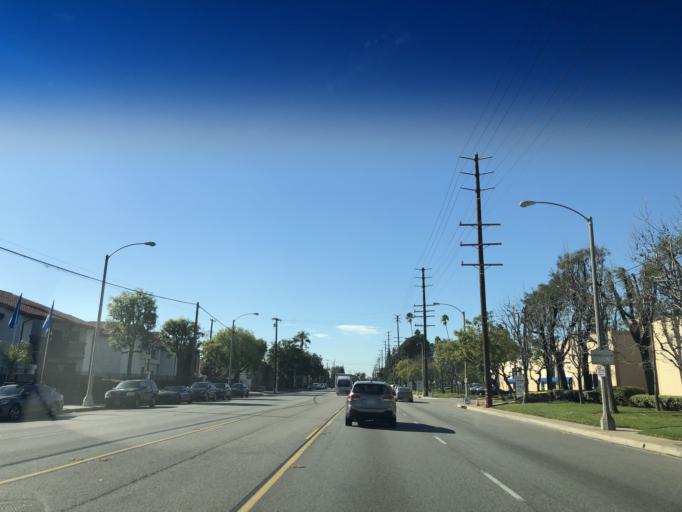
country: US
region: California
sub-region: Los Angeles County
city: Santa Fe Springs
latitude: 33.9354
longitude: -118.0767
